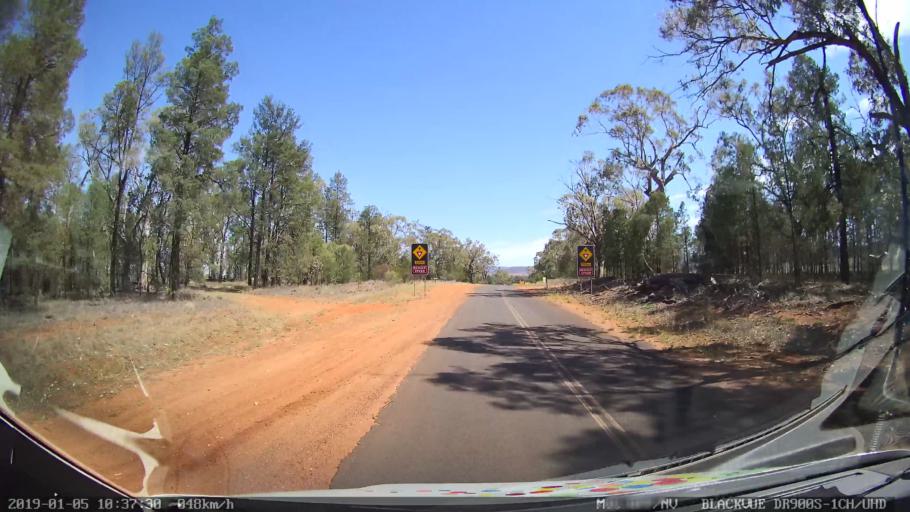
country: AU
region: New South Wales
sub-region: Gilgandra
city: Gilgandra
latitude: -31.4742
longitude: 148.9214
